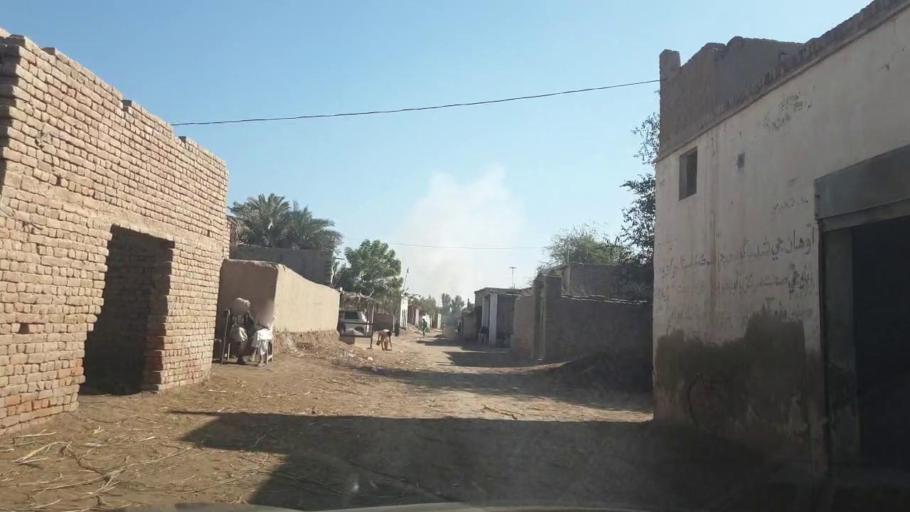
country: PK
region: Sindh
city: Mirpur Mathelo
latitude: 28.1408
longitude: 69.5311
